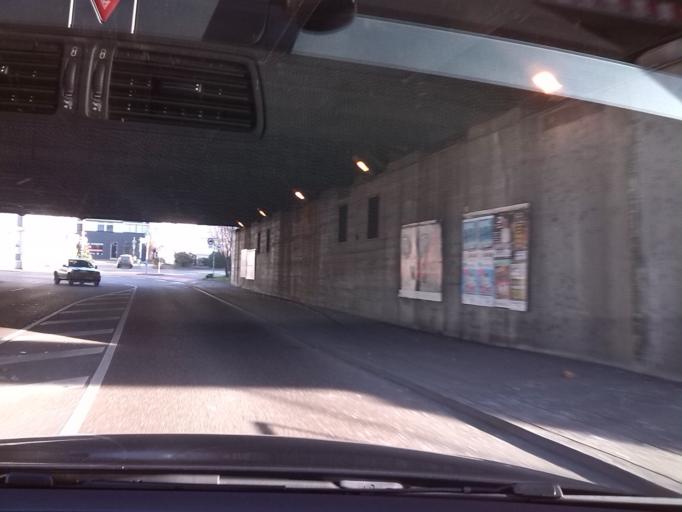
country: DE
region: Baden-Wuerttemberg
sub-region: Regierungsbezirk Stuttgart
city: Stuttgart-Ost
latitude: 48.7807
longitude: 9.2492
